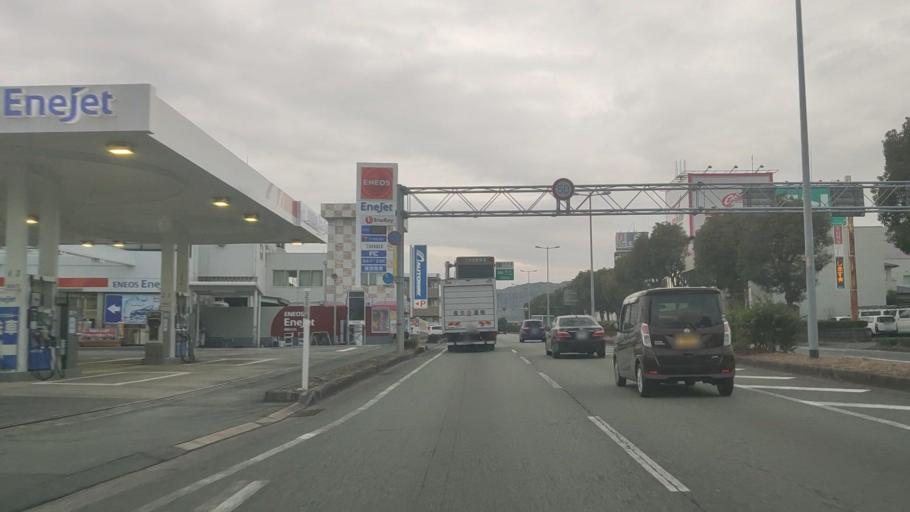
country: JP
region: Kumamoto
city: Kumamoto
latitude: 32.8307
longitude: 130.7718
